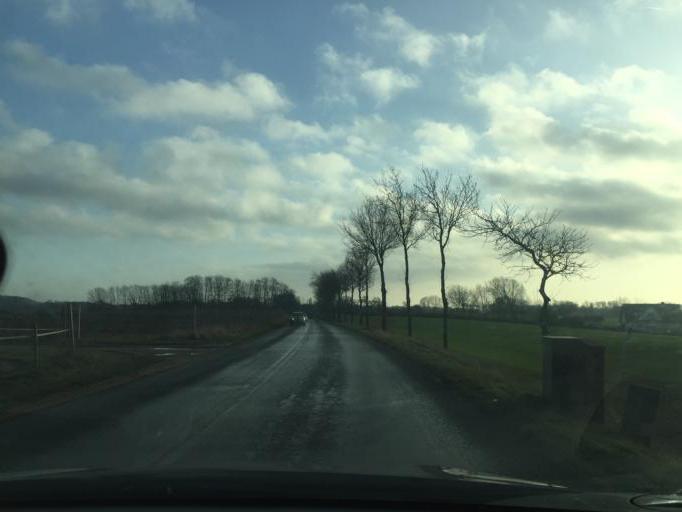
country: DK
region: South Denmark
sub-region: Odense Kommune
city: Bellinge
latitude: 55.1993
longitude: 10.3401
